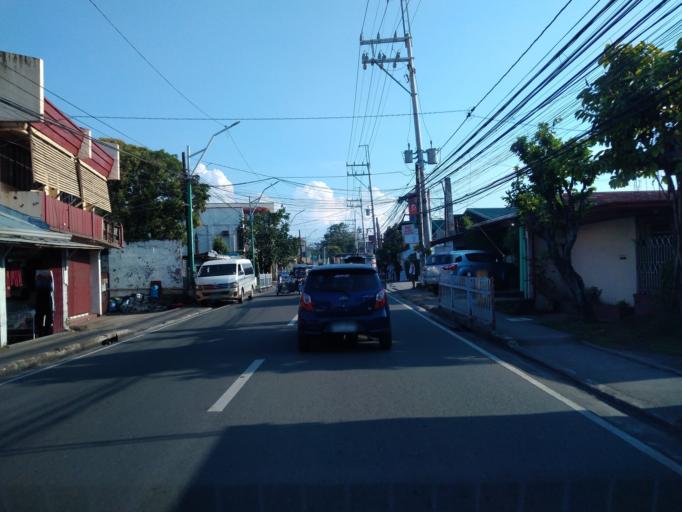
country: PH
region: Calabarzon
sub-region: Province of Laguna
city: Los Banos
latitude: 14.1762
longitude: 121.2428
